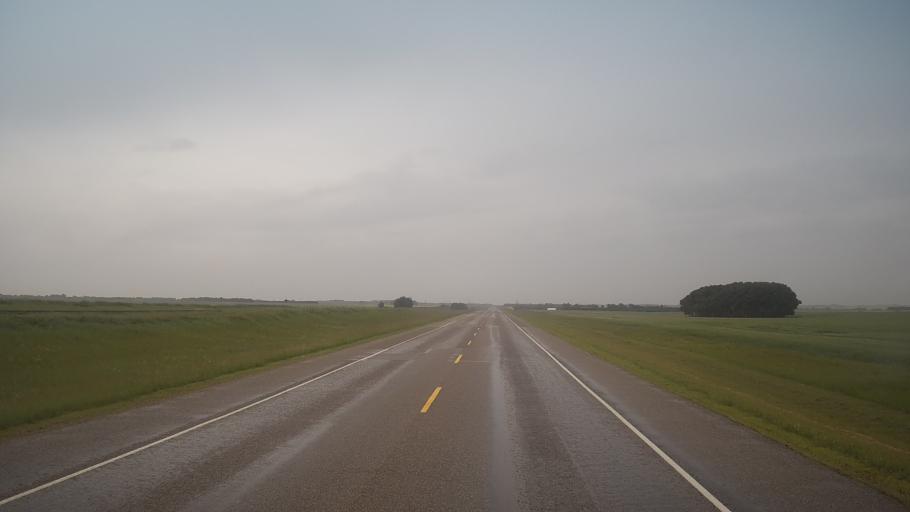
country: CA
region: Saskatchewan
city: Wilkie
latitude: 52.2261
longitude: -108.5291
